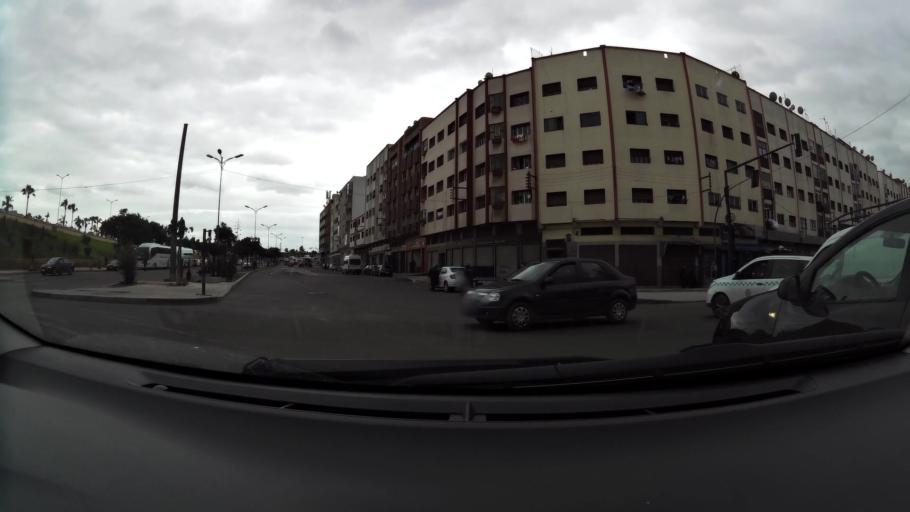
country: MA
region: Grand Casablanca
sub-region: Casablanca
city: Casablanca
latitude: 33.5716
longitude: -7.5801
